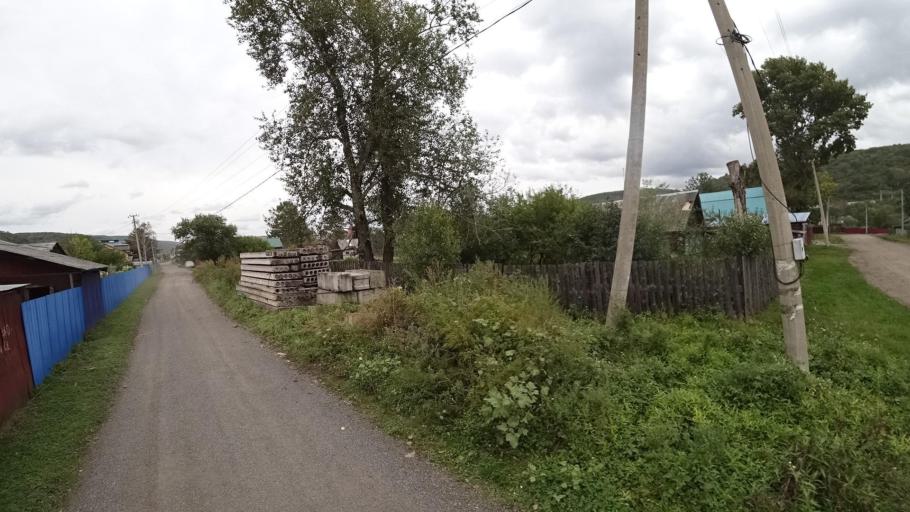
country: RU
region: Jewish Autonomous Oblast
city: Khingansk
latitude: 49.0049
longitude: 131.0520
